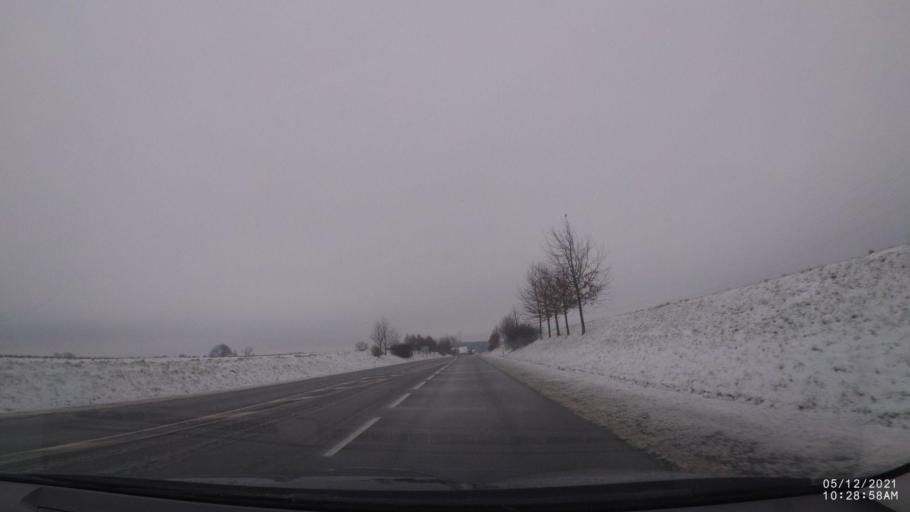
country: CZ
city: Vamberk
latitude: 50.1281
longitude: 16.2844
